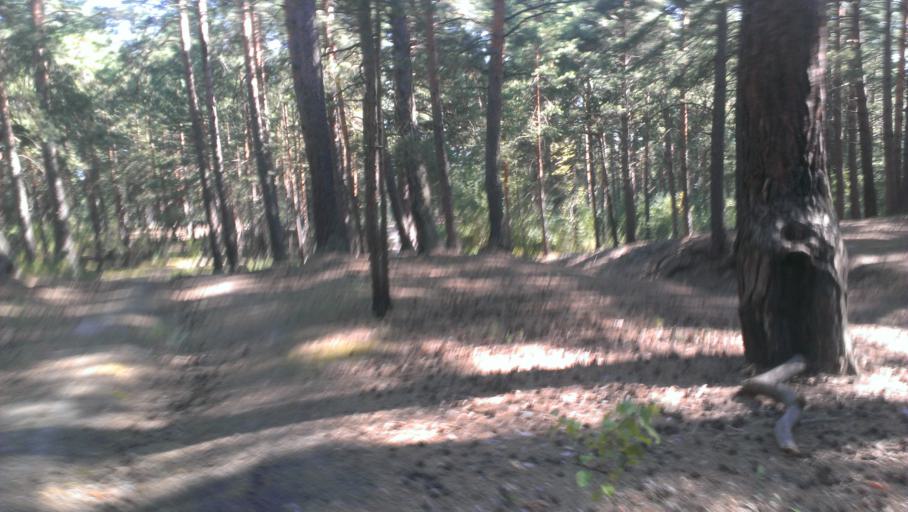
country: RU
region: Altai Krai
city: Yuzhnyy
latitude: 53.3165
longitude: 83.6883
